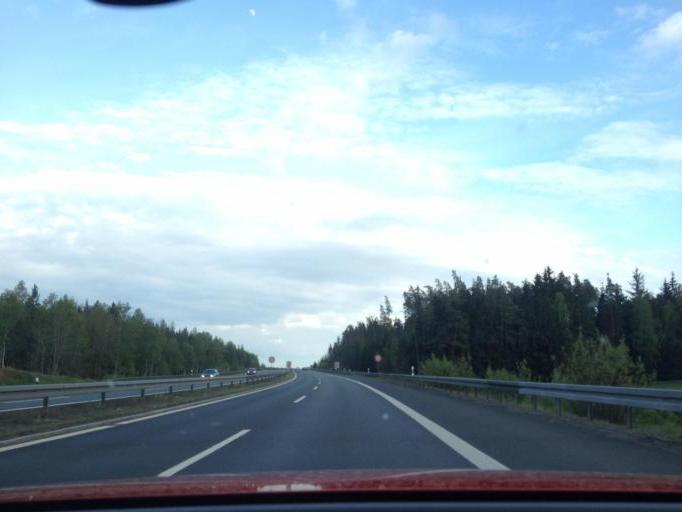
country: DE
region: Bavaria
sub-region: Upper Palatinate
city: Pechbrunn
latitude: 49.9657
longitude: 12.1828
